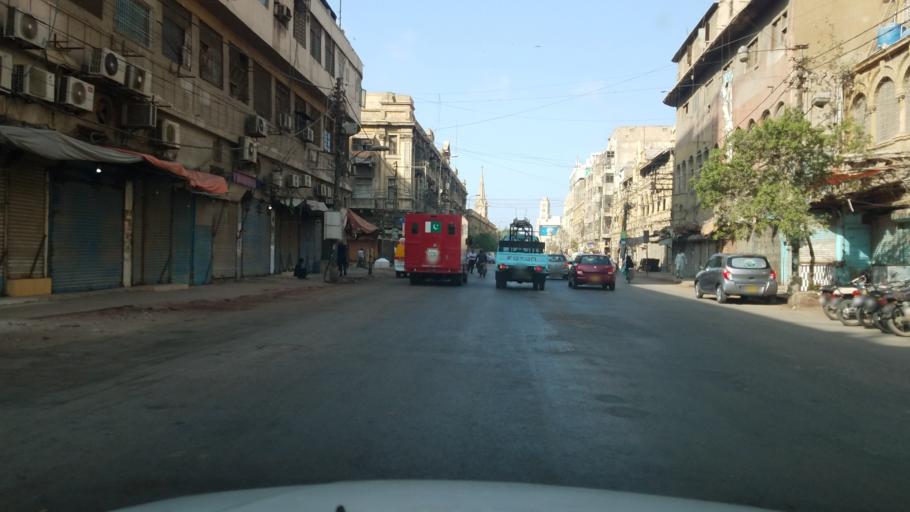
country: PK
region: Sindh
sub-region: Karachi District
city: Karachi
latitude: 24.8504
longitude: 66.9997
